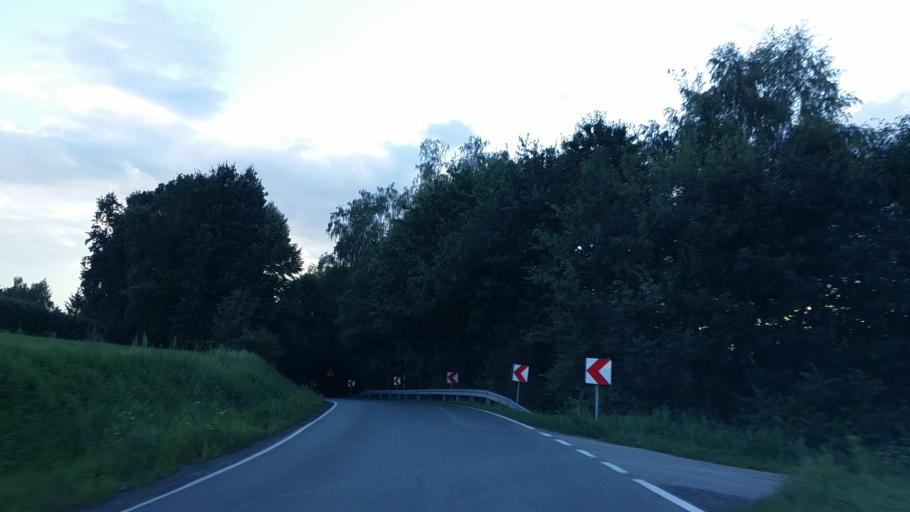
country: PL
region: Lesser Poland Voivodeship
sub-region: Powiat oswiecimski
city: Przeciszow
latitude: 49.9896
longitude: 19.3551
